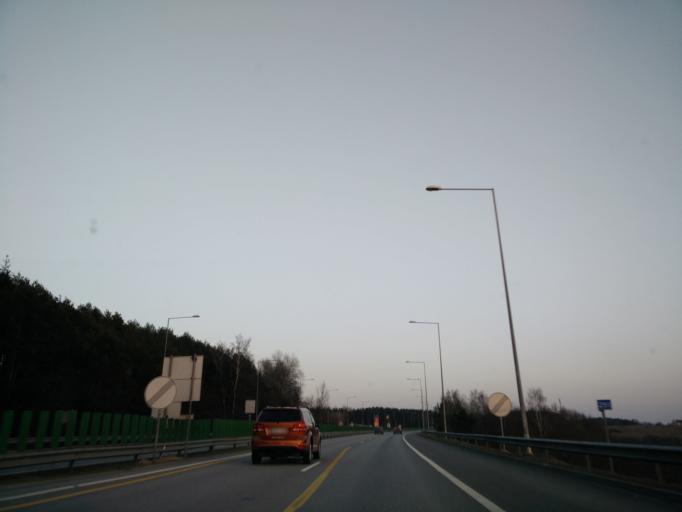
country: LT
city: Grigiskes
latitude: 54.6885
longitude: 25.0481
